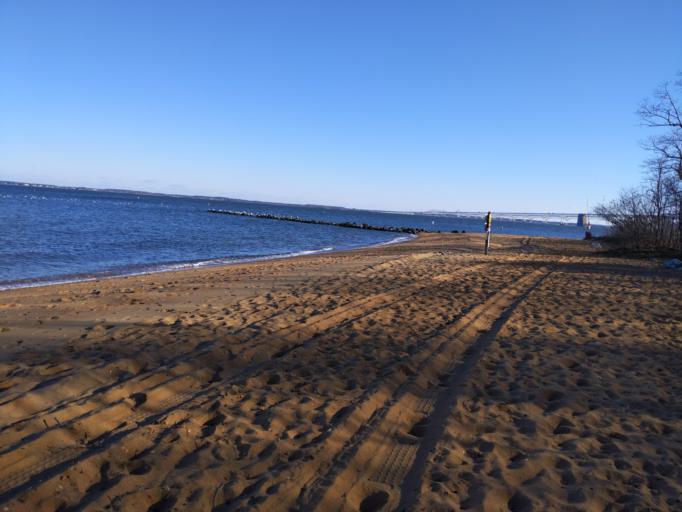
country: US
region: Maryland
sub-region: Anne Arundel County
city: Cape Saint Claire
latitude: 39.0145
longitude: -76.3957
